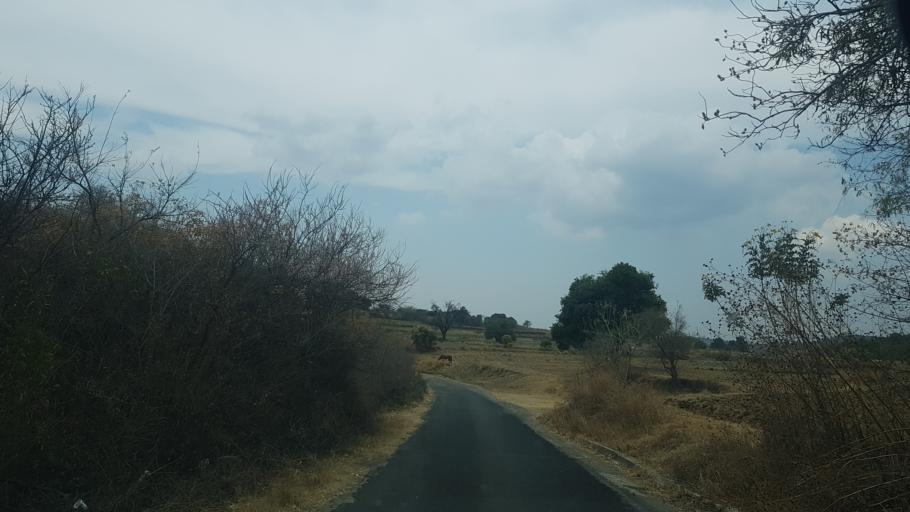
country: MX
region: Puebla
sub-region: Atzitzihuacan
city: Santiago Atzitzihuacan
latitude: 18.8441
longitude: -98.6095
